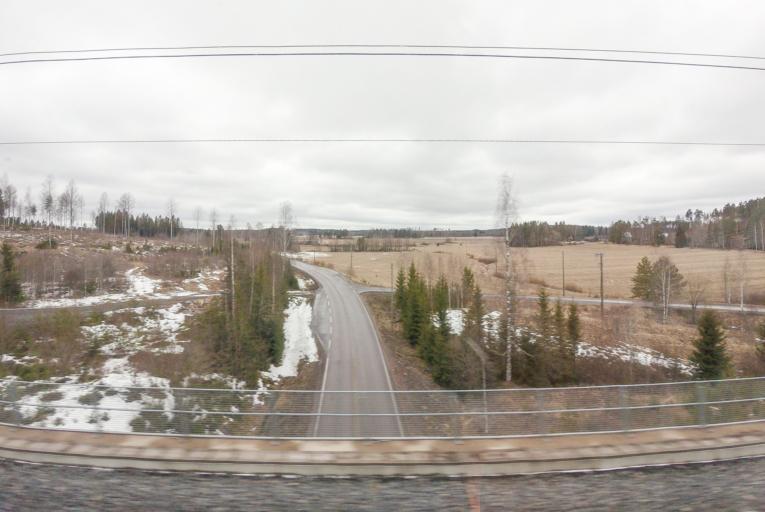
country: FI
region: Uusimaa
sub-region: Helsinki
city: Maentsaelae
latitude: 60.7022
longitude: 25.4066
